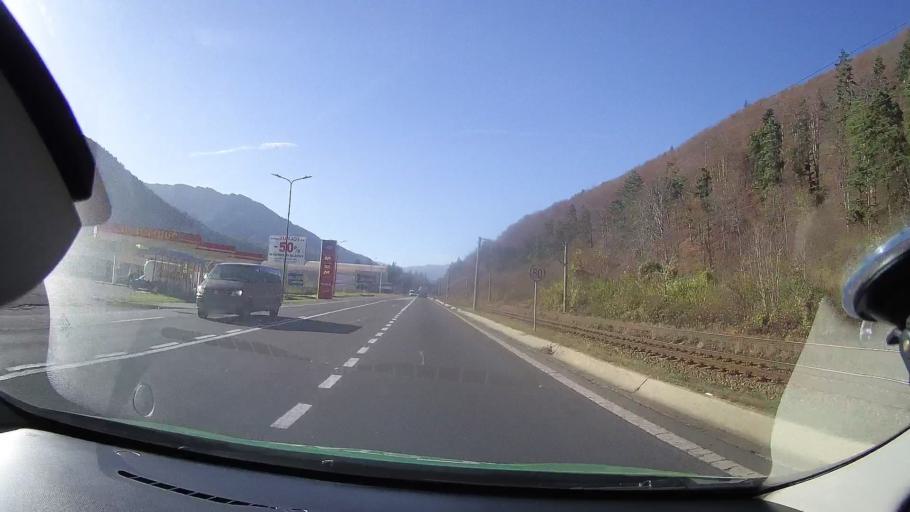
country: RO
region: Brasov
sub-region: Municipiul Sacele
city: Sacele
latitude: 45.6048
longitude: 25.6507
